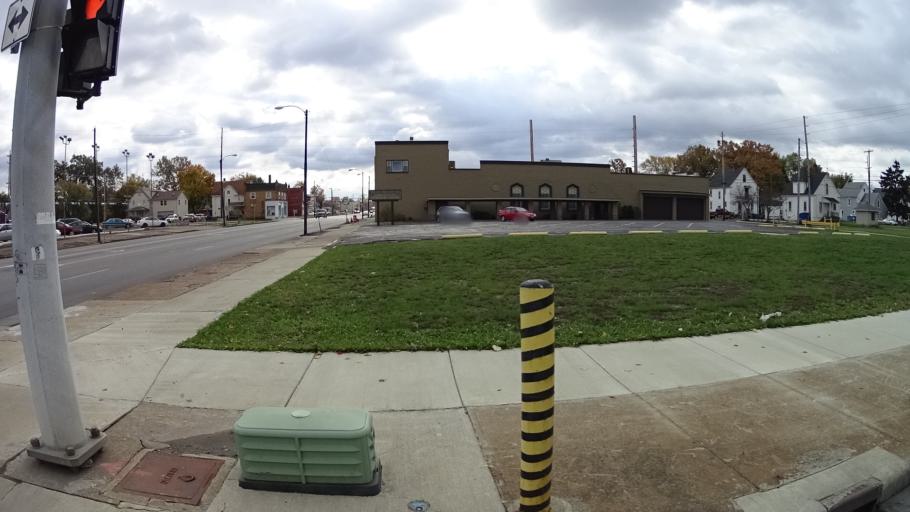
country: US
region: Ohio
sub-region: Lorain County
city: Lorain
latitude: 41.4515
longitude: -82.1663
